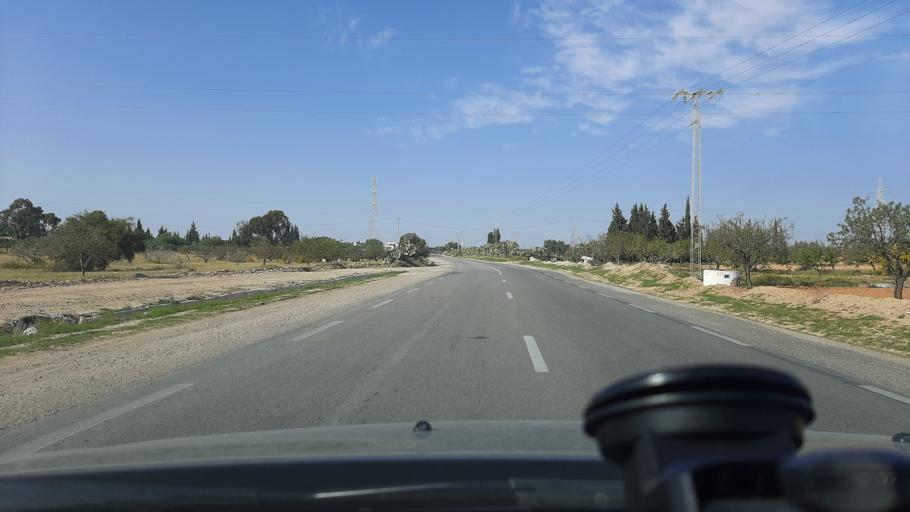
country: TN
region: Safaqis
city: Sfax
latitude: 34.8093
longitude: 10.6231
